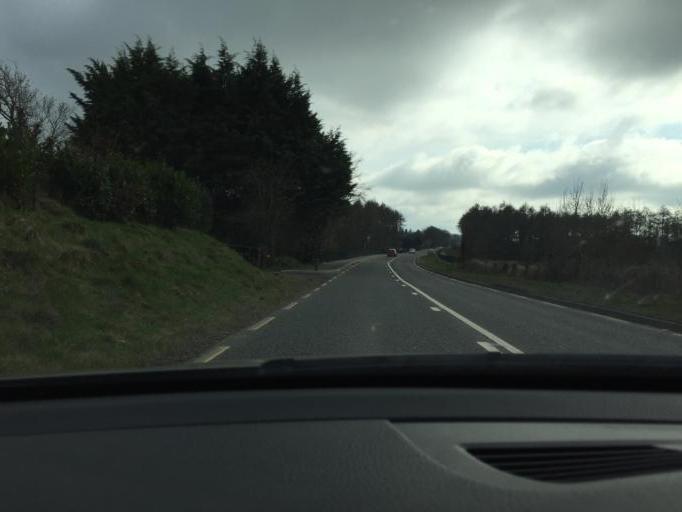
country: IE
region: Leinster
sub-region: Wicklow
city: Blessington
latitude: 53.1581
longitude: -6.5518
